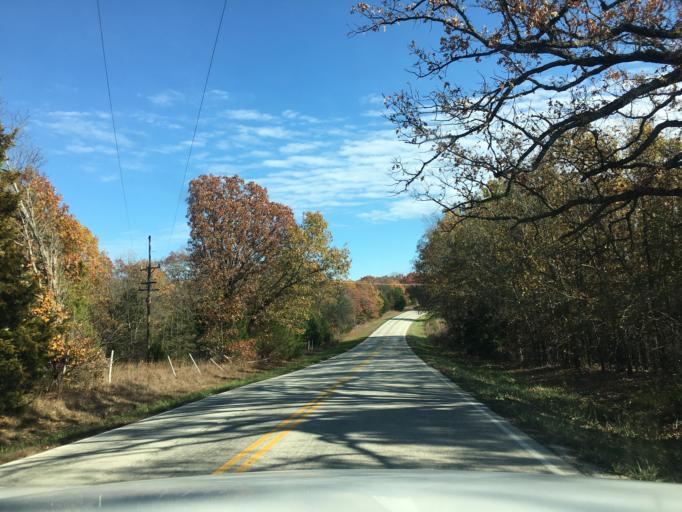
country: US
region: Missouri
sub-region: Maries County
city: Belle
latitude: 38.3120
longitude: -91.7437
